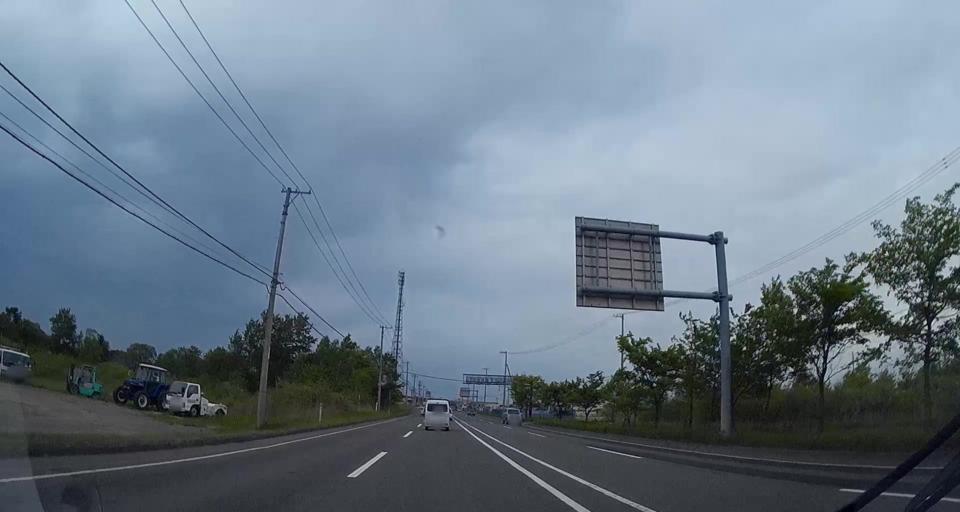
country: JP
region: Hokkaido
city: Tomakomai
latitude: 42.6754
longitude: 141.7087
